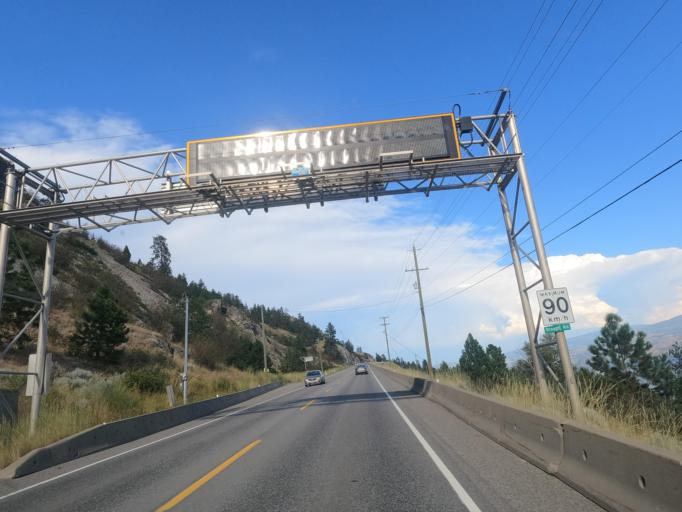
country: CA
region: British Columbia
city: Peachland
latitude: 49.7966
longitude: -119.6919
